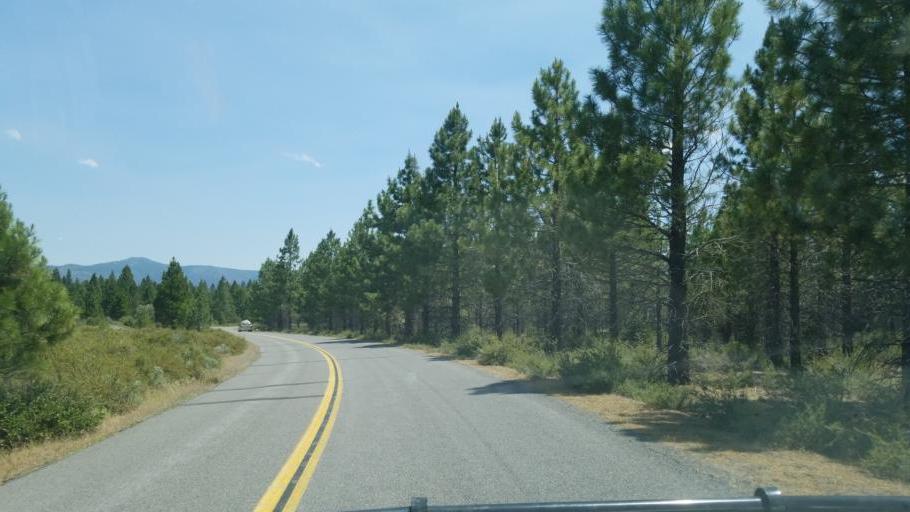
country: US
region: California
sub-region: Lassen County
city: Susanville
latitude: 40.5779
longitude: -120.8475
